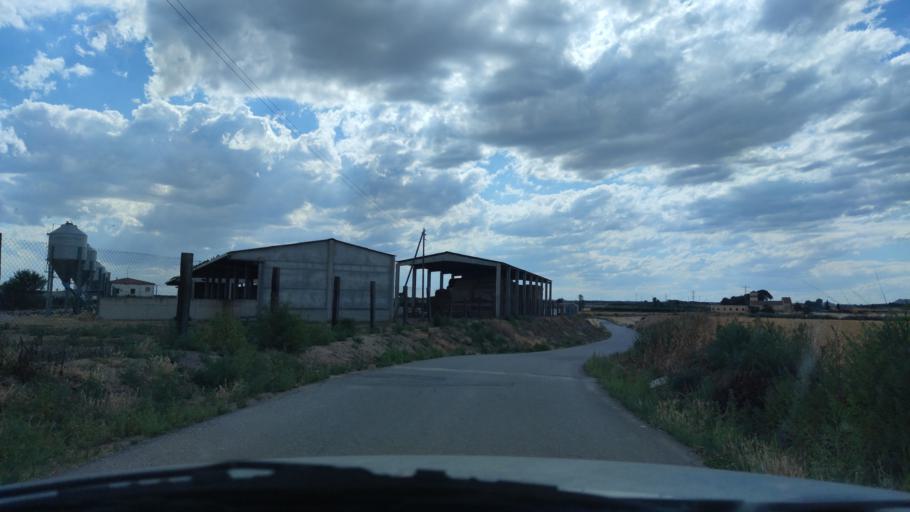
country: ES
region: Catalonia
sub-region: Provincia de Lleida
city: Lleida
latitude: 41.5976
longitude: 0.5678
